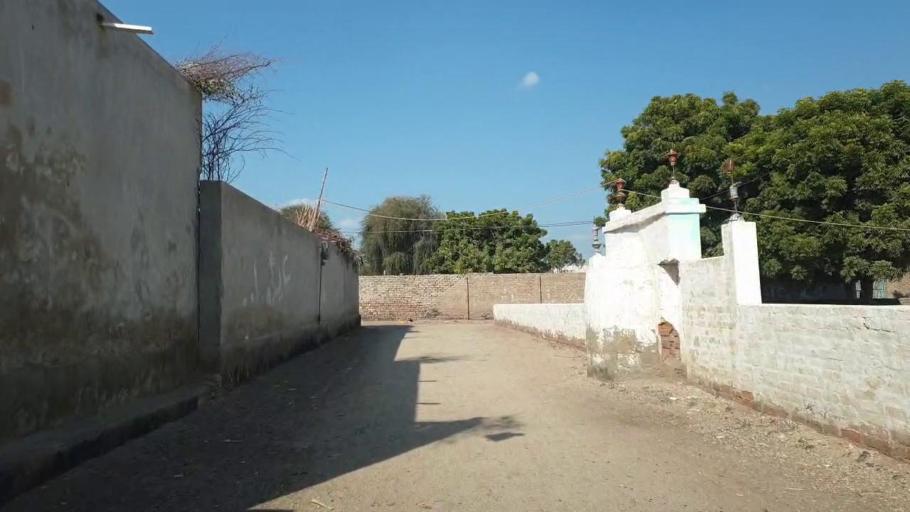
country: PK
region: Sindh
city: Shahpur Chakar
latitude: 26.1008
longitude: 68.5660
